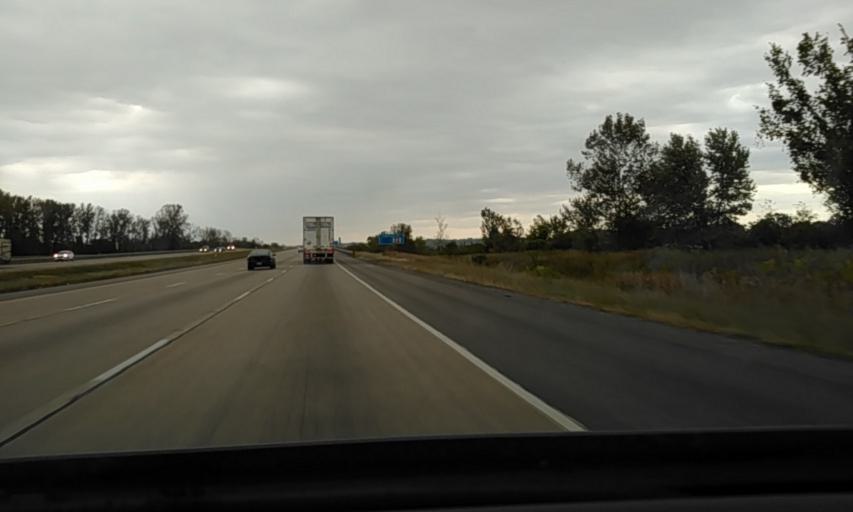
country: US
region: Illinois
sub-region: Saint Clair County
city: Caseyville
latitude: 38.6375
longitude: -90.0563
